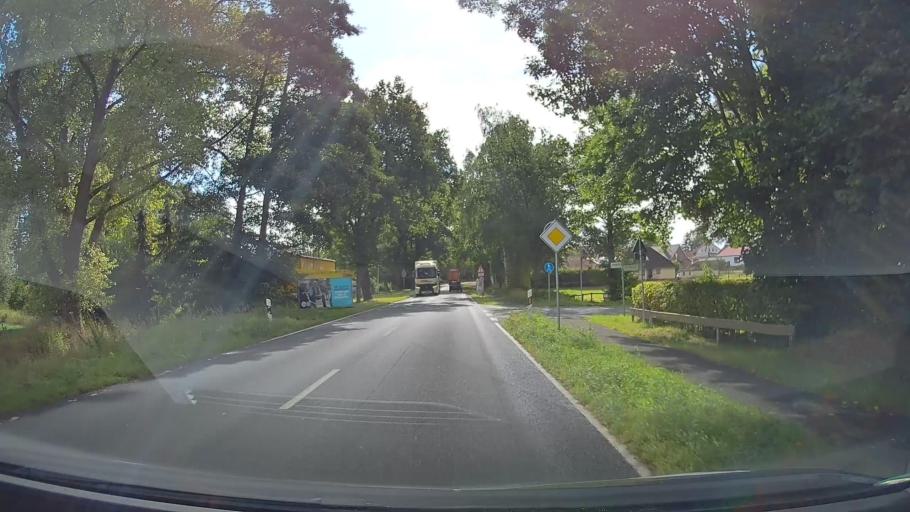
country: DE
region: Lower Saxony
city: Rhade
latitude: 53.3305
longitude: 9.1138
